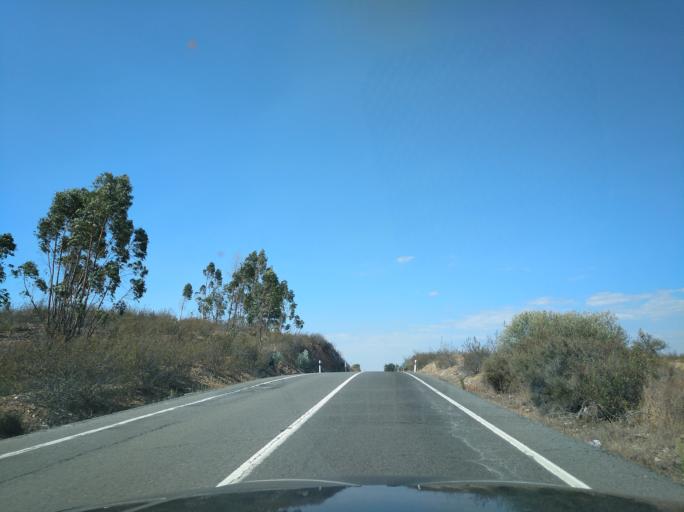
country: ES
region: Andalusia
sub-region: Provincia de Huelva
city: San Bartolome de la Torre
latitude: 37.4937
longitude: -7.1324
